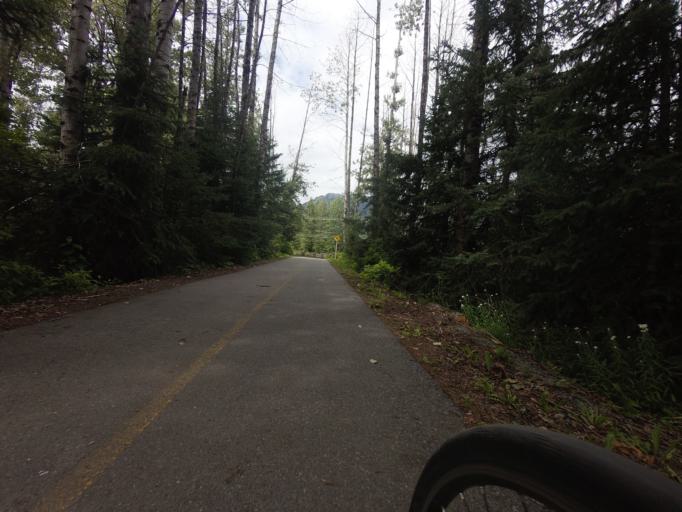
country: CA
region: British Columbia
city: Whistler
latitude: 50.1354
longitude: -122.9520
